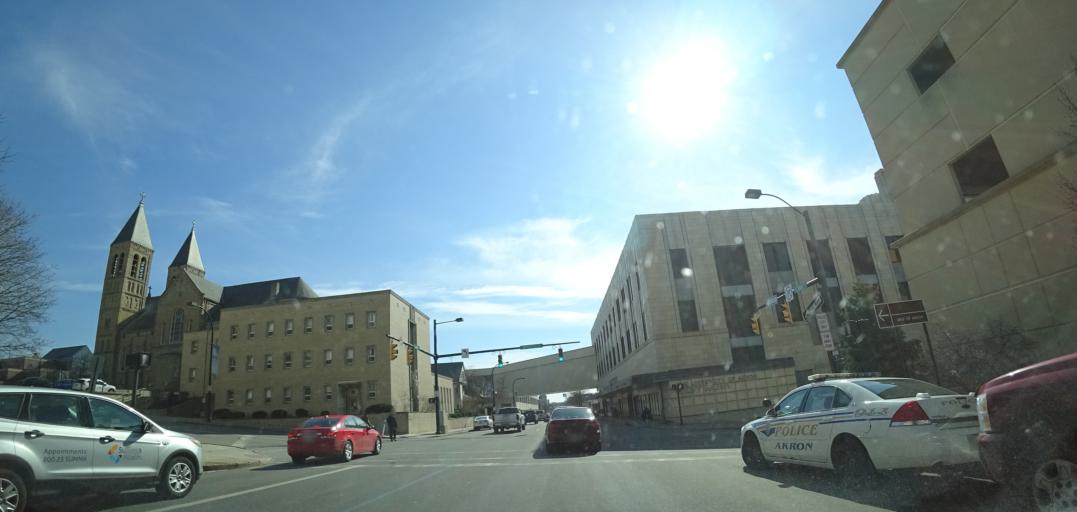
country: US
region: Ohio
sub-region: Summit County
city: Akron
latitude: 41.0792
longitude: -81.5187
